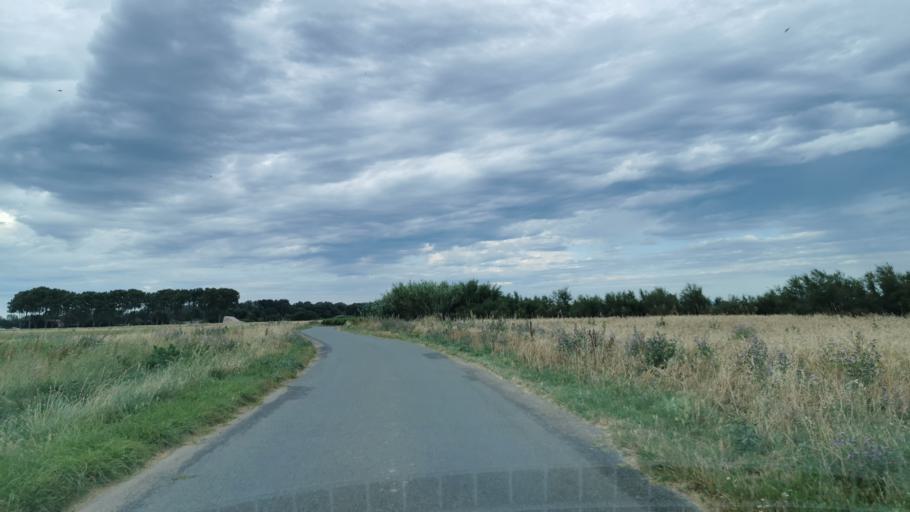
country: FR
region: Languedoc-Roussillon
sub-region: Departement de l'Aude
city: Moussan
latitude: 43.2359
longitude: 2.9946
